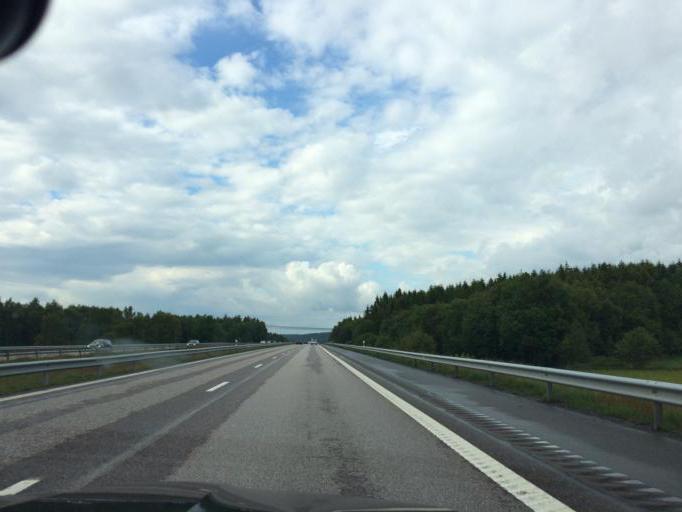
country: SE
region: Halland
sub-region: Kungsbacka Kommun
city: Frillesas
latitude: 57.2775
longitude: 12.2157
